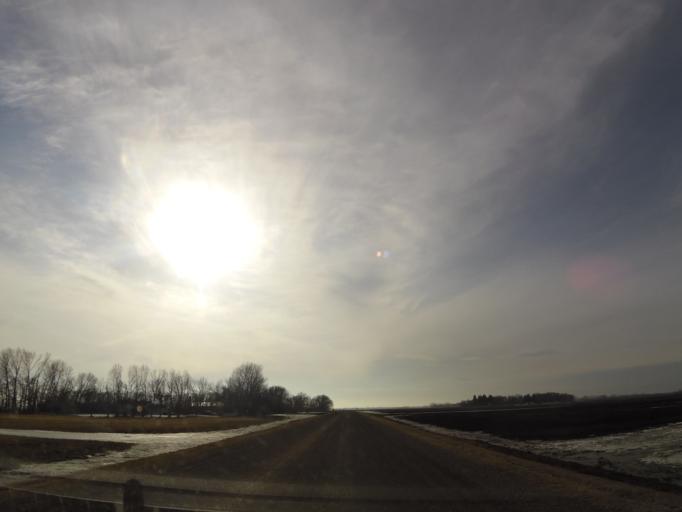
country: US
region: North Dakota
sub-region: Walsh County
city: Grafton
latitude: 48.4265
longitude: -97.2208
